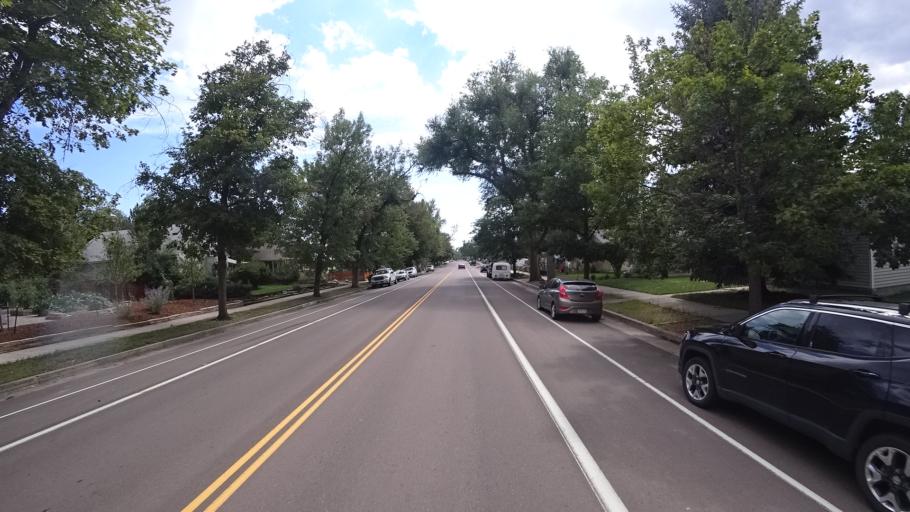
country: US
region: Colorado
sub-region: El Paso County
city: Colorado Springs
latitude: 38.8486
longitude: -104.8075
